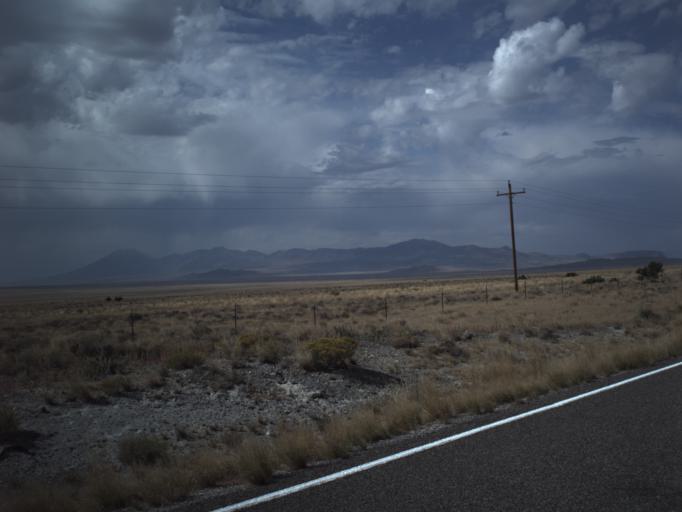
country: US
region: Utah
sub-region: Tooele County
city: Wendover
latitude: 41.4362
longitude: -113.7498
